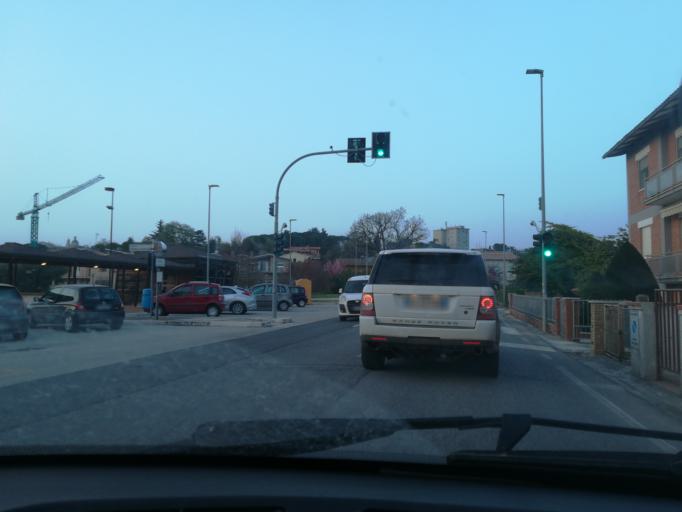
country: IT
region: The Marches
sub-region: Provincia di Macerata
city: Macerata
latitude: 43.2864
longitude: 13.4513
